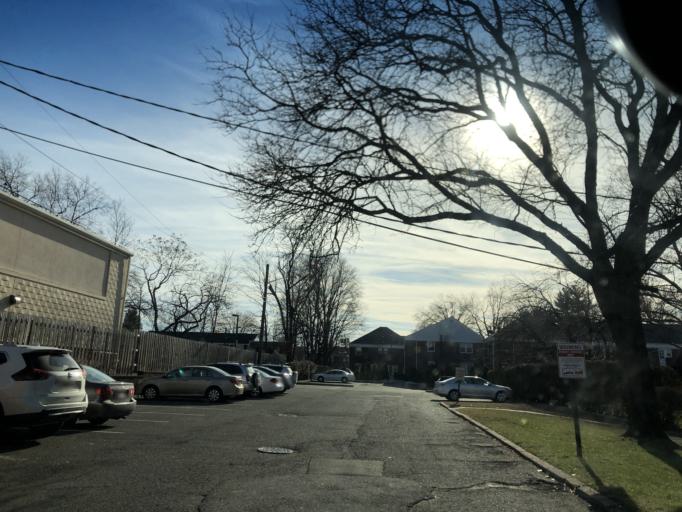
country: US
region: New Jersey
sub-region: Bergen County
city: Elmwood Park
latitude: 40.9176
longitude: -74.1284
